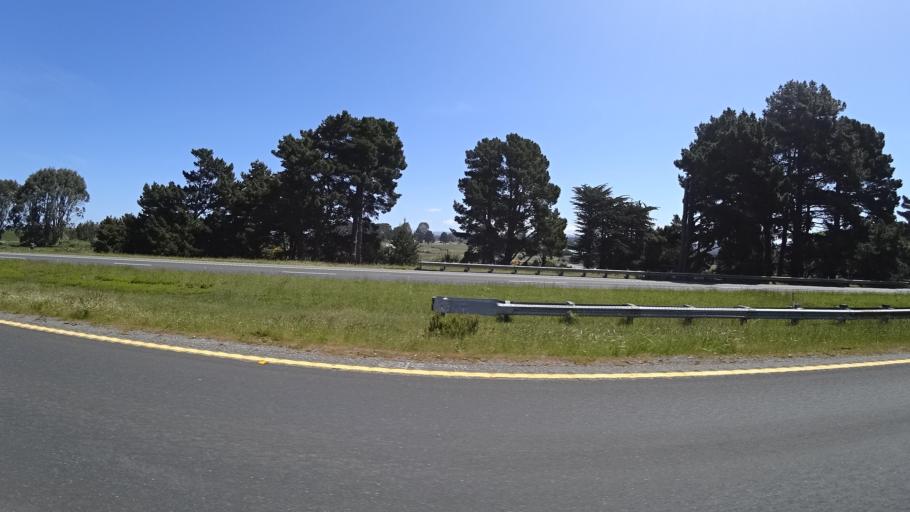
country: US
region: California
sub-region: Humboldt County
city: McKinleyville
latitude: 40.9695
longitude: -124.1161
